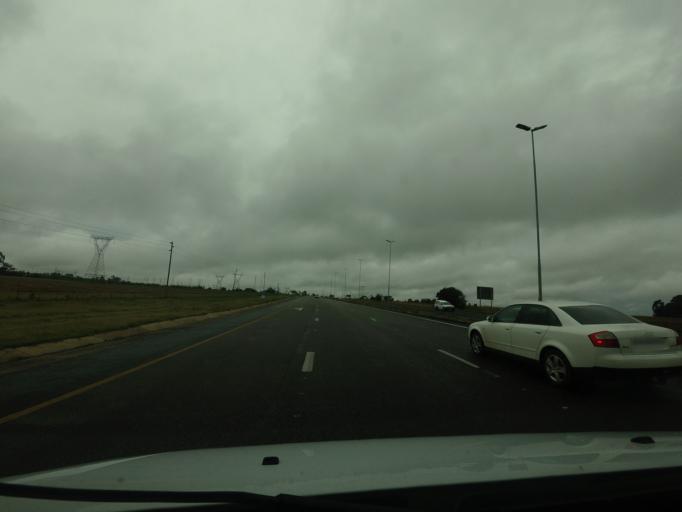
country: ZA
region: Mpumalanga
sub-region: Nkangala District Municipality
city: Belfast
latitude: -25.8152
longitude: 29.8882
